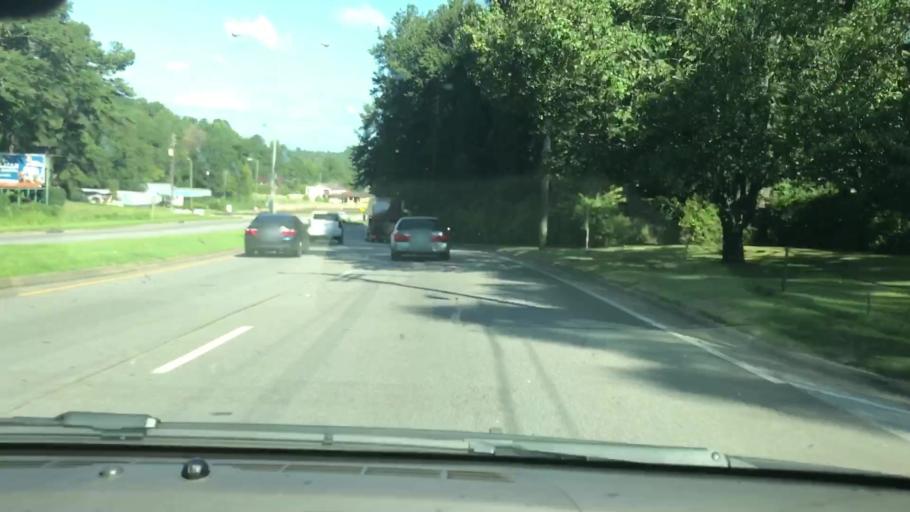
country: US
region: Alabama
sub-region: Barbour County
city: Eufaula
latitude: 31.9038
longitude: -85.1469
